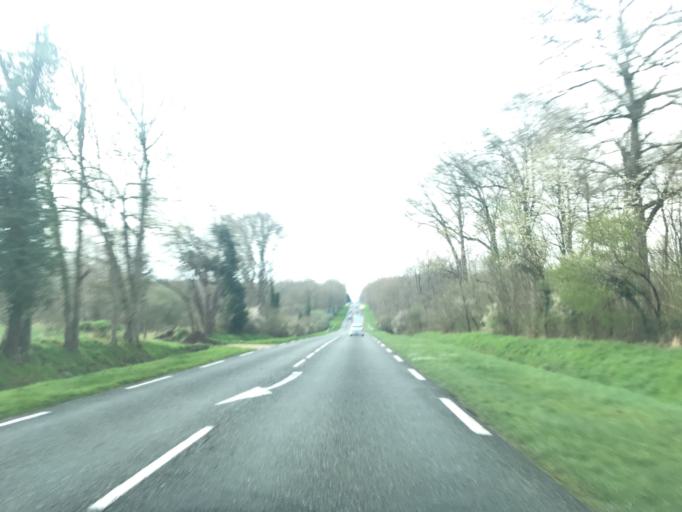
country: FR
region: Centre
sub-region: Departement du Loiret
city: Nevoy
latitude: 47.7262
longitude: 2.5781
